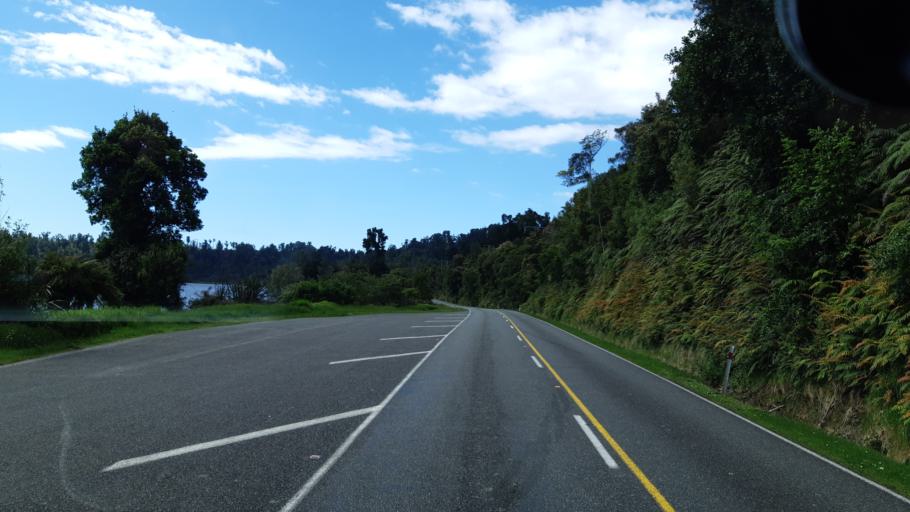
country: NZ
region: West Coast
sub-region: Westland District
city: Hokitika
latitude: -43.0583
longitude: 170.6354
